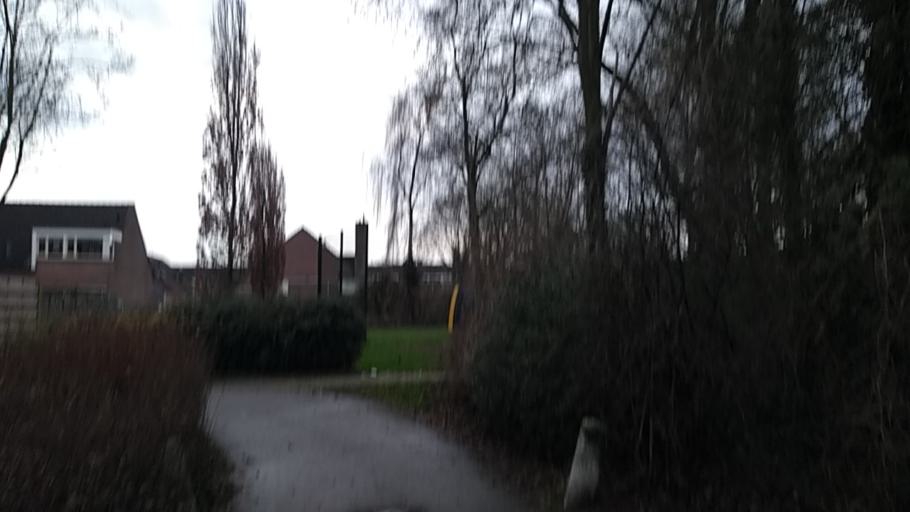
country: NL
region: Overijssel
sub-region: Gemeente Almelo
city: Almelo
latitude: 52.3784
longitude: 6.6854
